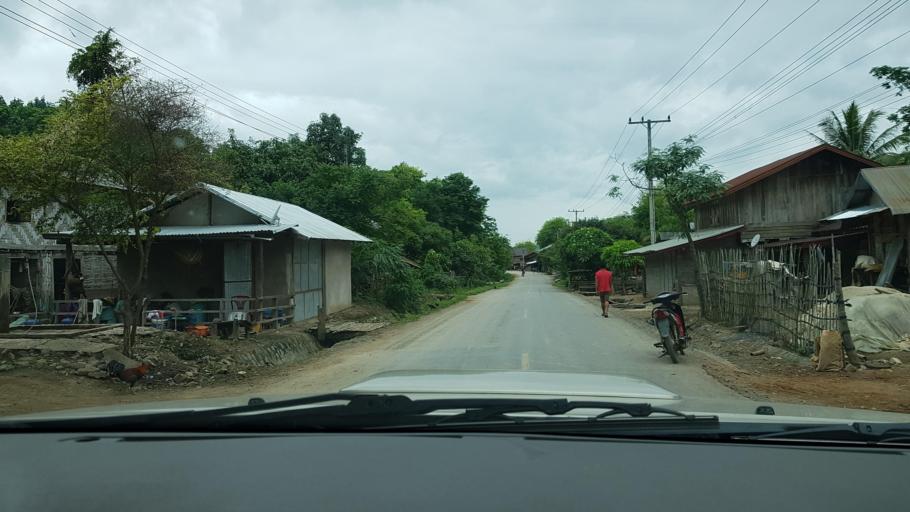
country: LA
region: Loungnamtha
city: Muang Nale
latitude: 20.2662
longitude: 101.5964
